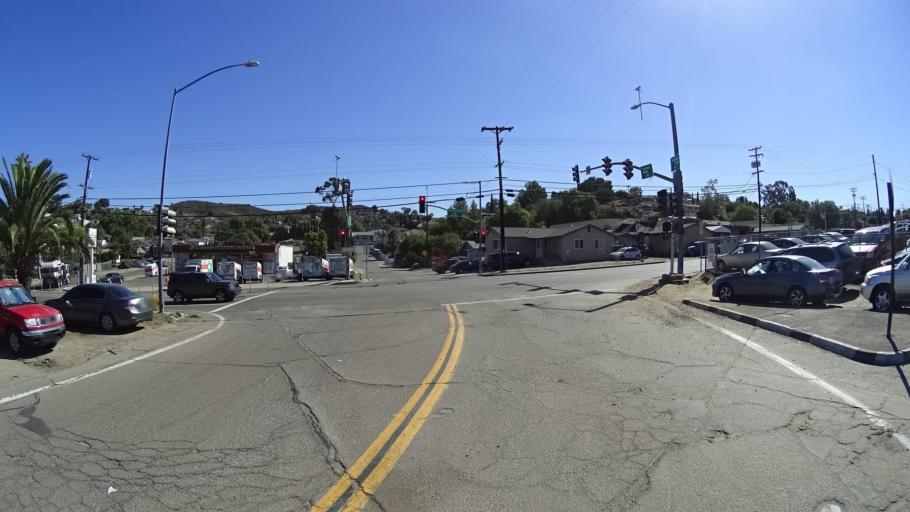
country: US
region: California
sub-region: San Diego County
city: Winter Gardens
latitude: 32.8385
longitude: -116.9339
